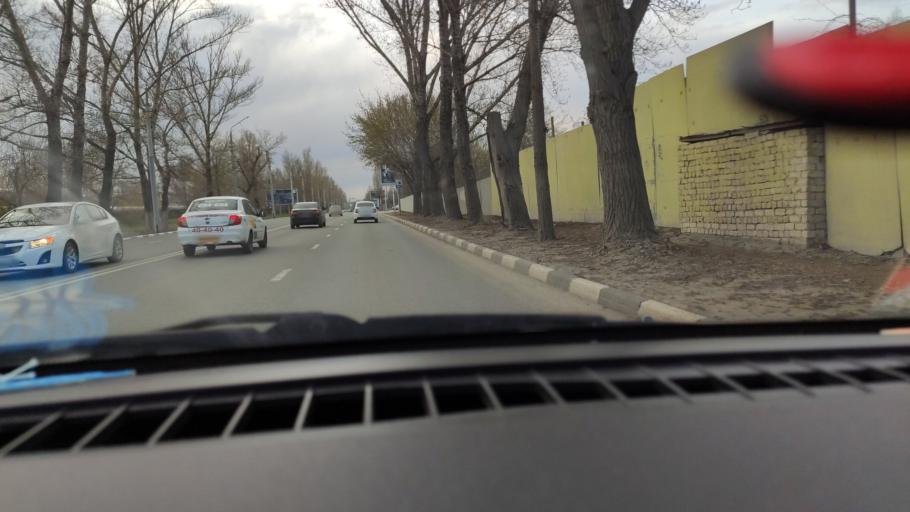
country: RU
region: Saratov
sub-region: Saratovskiy Rayon
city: Saratov
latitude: 51.5757
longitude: 45.9887
